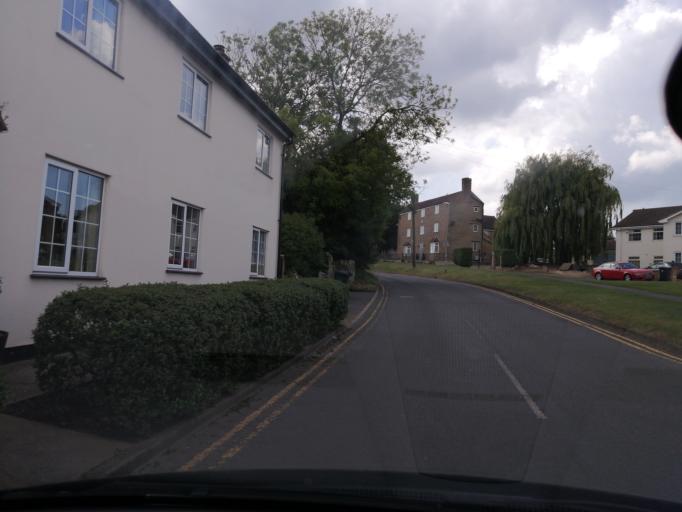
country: GB
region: England
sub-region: Cambridgeshire
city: Yaxley
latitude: 52.5112
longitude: -0.2631
